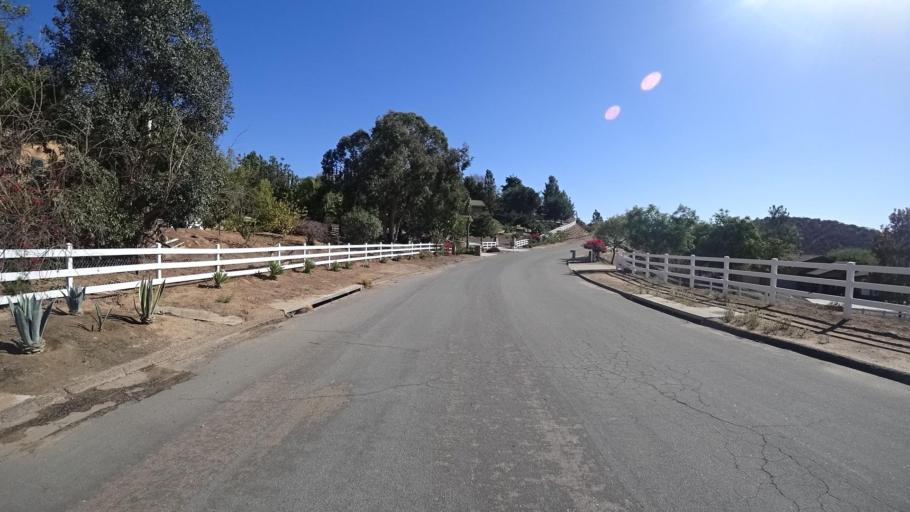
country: US
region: California
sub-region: San Diego County
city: Lakeside
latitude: 32.8674
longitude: -116.8805
